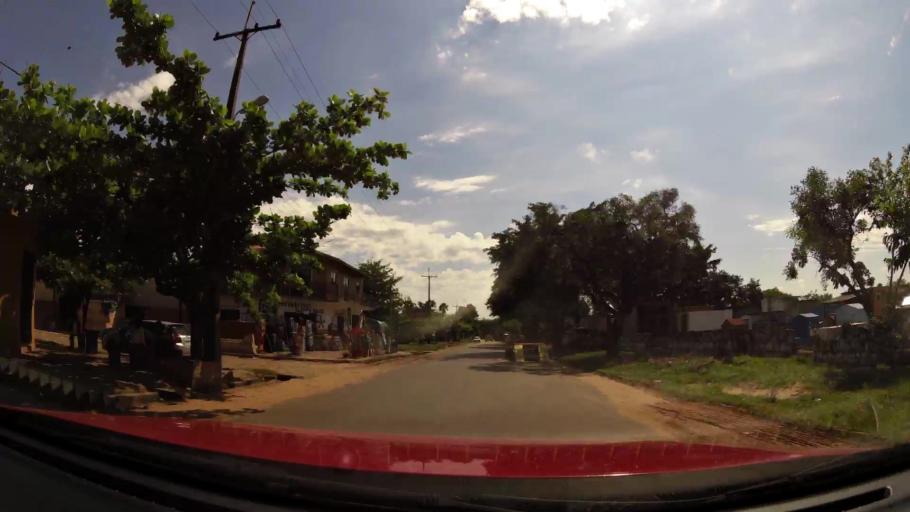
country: PY
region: Central
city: Limpio
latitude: -25.2527
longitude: -57.4928
